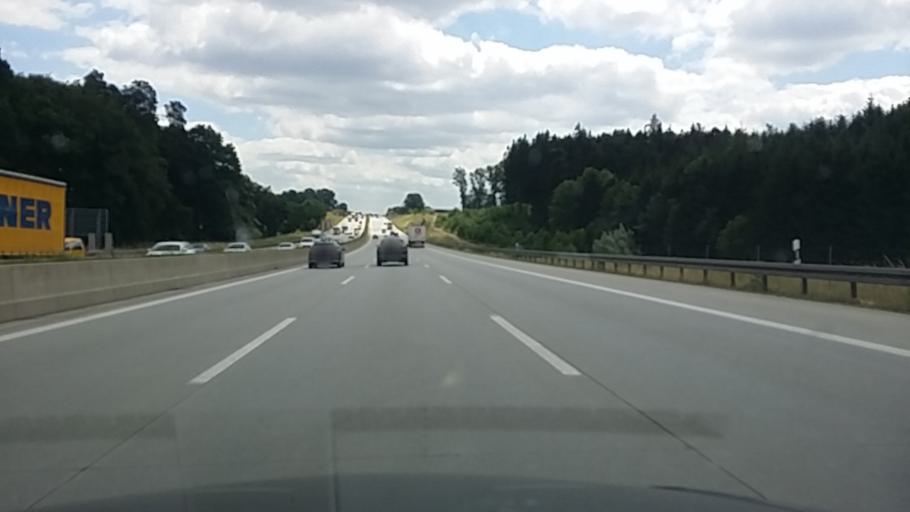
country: DE
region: Bavaria
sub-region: Upper Bavaria
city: Odelzhausen
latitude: 48.3263
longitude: 11.1733
